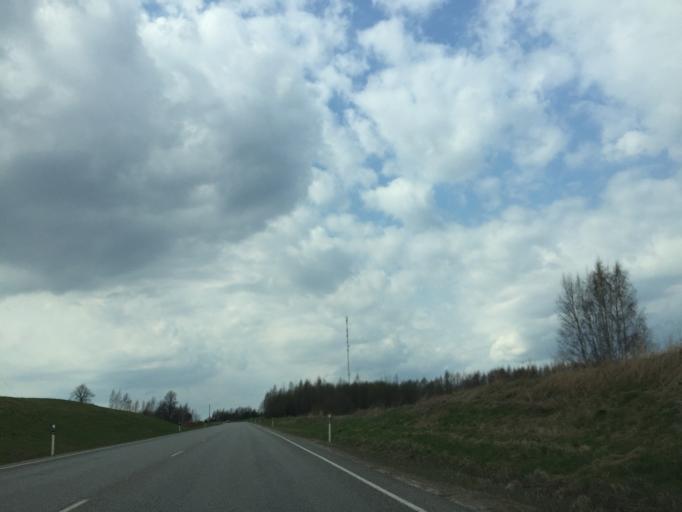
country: EE
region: Vorumaa
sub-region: Voru linn
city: Voru
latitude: 57.7439
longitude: 27.2527
